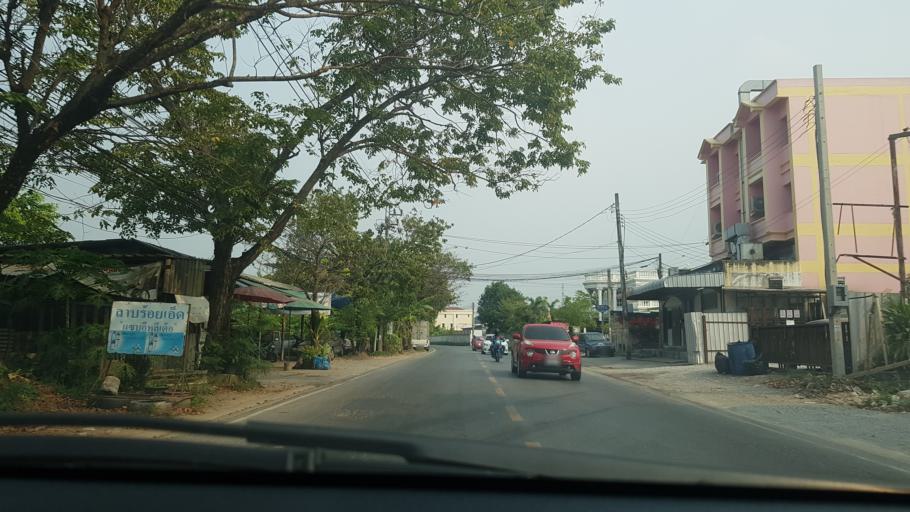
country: TH
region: Bangkok
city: Phasi Charoen
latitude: 13.7554
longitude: 100.4003
